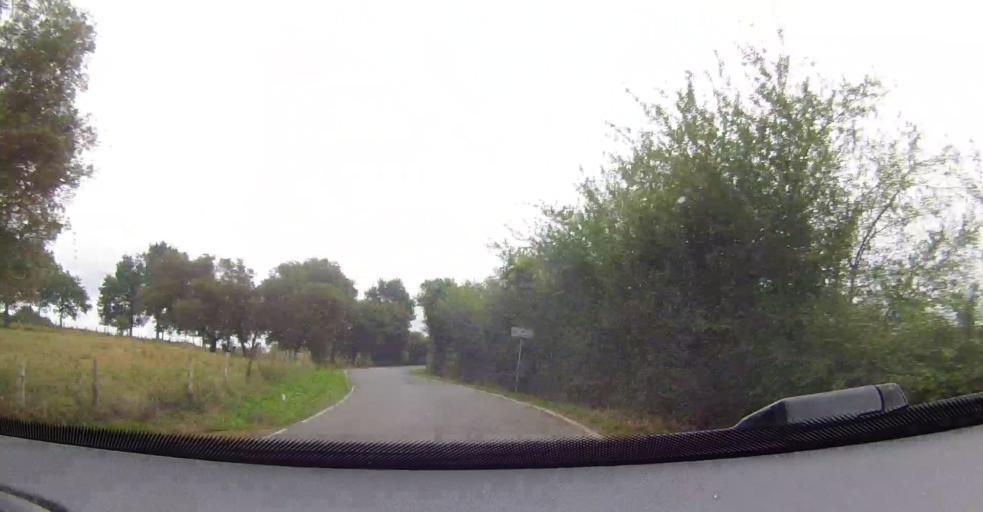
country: ES
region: Basque Country
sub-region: Bizkaia
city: Urrestieta
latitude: 43.2339
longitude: -3.1881
